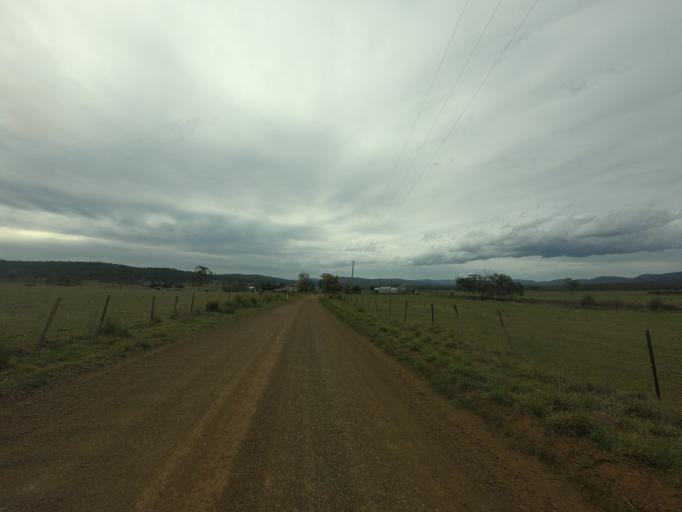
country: AU
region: Tasmania
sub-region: Break O'Day
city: St Helens
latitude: -41.9634
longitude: 148.0719
